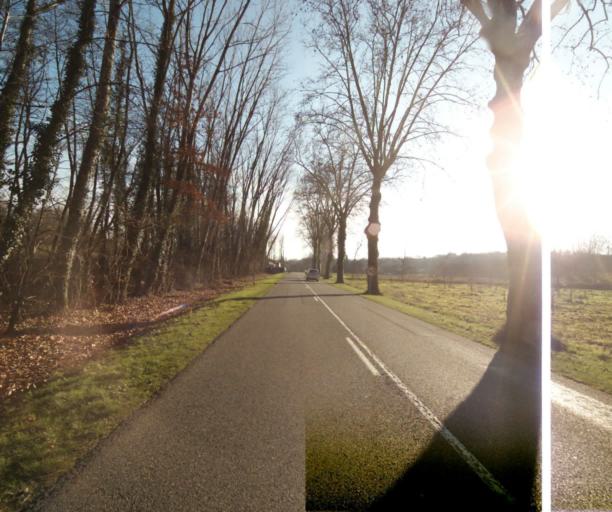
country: FR
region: Midi-Pyrenees
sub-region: Departement du Tarn-et-Garonne
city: Moissac
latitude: 44.1278
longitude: 1.1038
